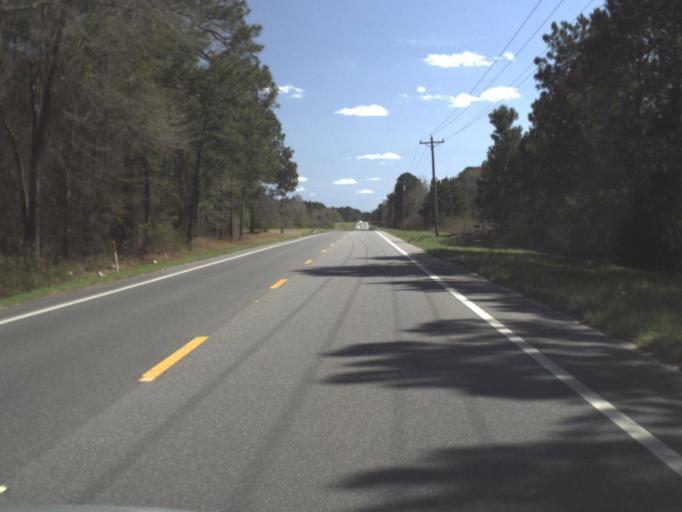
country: US
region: Florida
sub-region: Gadsden County
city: Gretna
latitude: 30.6453
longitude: -84.6788
